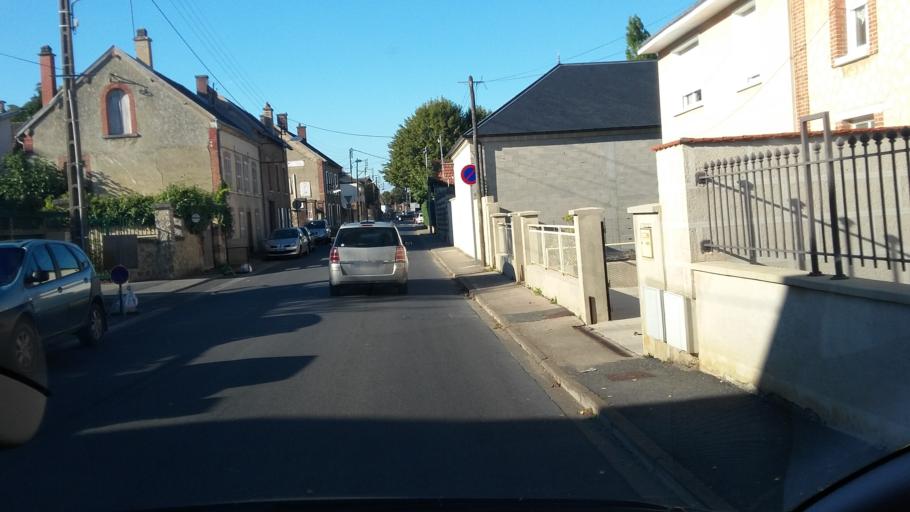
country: FR
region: Champagne-Ardenne
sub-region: Departement de la Marne
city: Avize
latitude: 48.9680
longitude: 4.0080
